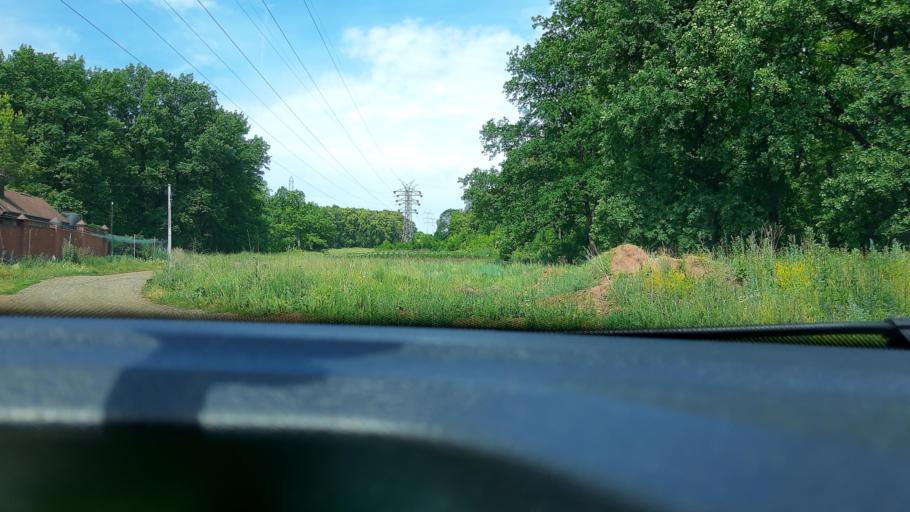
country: RU
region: Bashkortostan
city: Avdon
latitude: 54.6228
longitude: 55.6366
